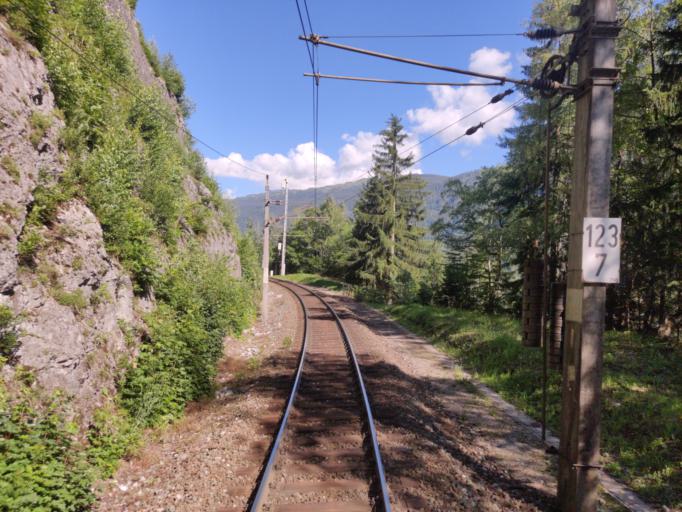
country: AT
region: Vorarlberg
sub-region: Politischer Bezirk Bludenz
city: Dalaas
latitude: 47.1311
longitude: 9.9623
